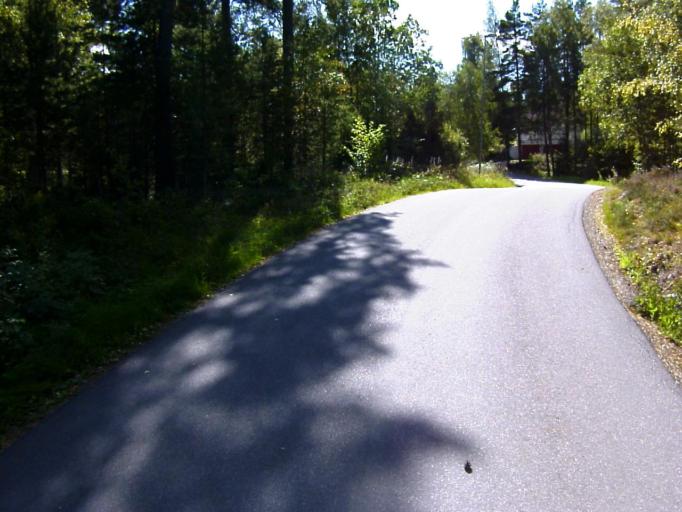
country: SE
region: Soedermanland
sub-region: Eskilstuna Kommun
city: Eskilstuna
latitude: 59.3601
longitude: 16.5553
